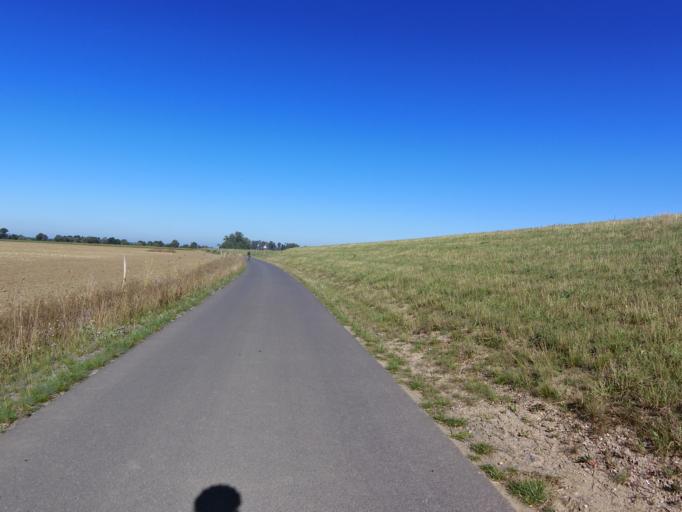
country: DE
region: Saxony
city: Torgau
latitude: 51.6138
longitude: 12.9915
